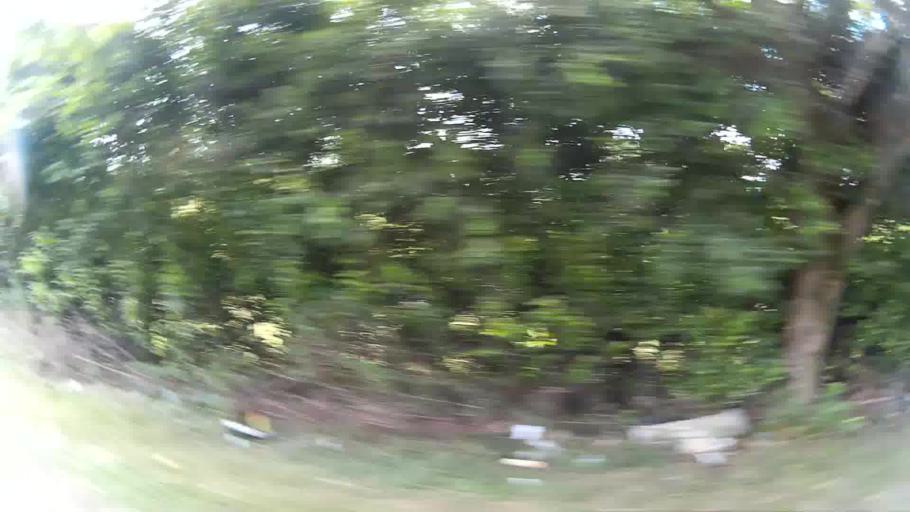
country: CO
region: Risaralda
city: La Virginia
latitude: 4.8318
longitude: -75.8491
